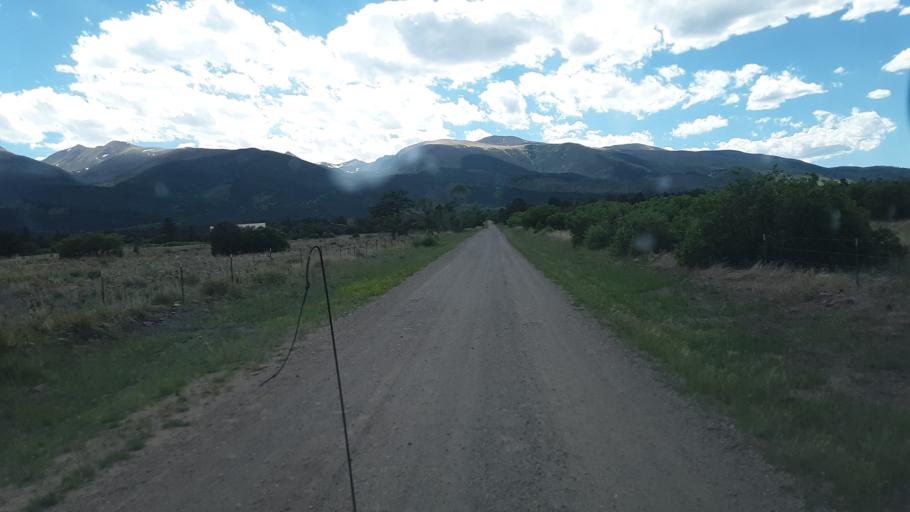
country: US
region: Colorado
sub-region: Custer County
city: Westcliffe
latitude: 38.2252
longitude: -105.6011
